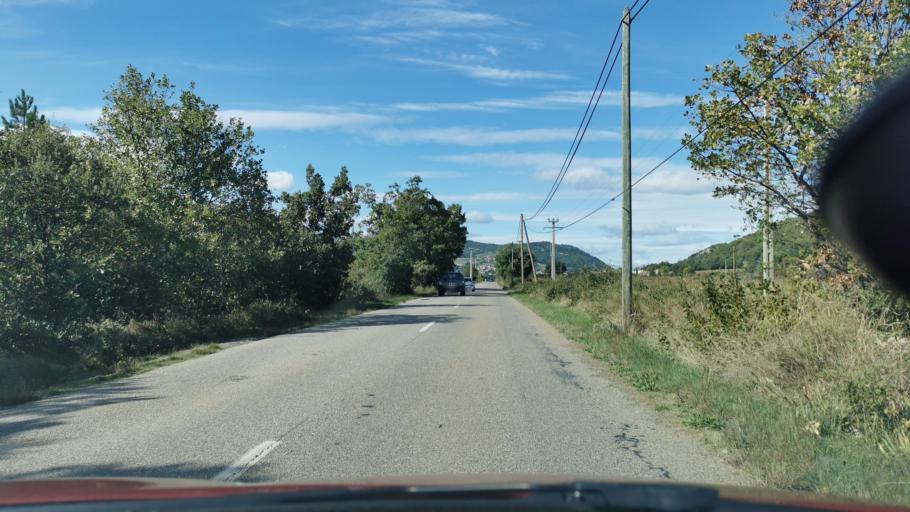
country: FR
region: Provence-Alpes-Cote d'Azur
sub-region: Departement des Alpes-de-Haute-Provence
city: Peipin
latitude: 44.1624
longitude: 5.9643
